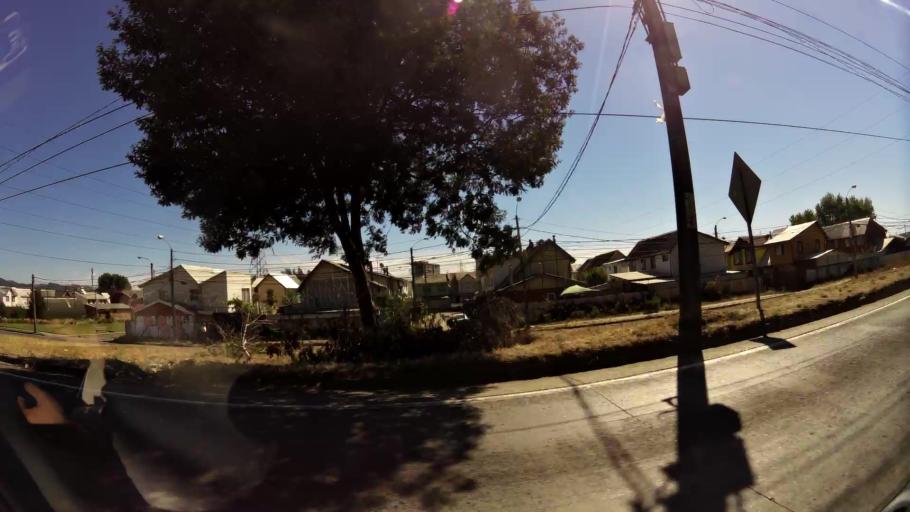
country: CL
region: Biobio
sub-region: Provincia de Concepcion
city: Concepcion
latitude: -36.8028
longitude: -73.0255
